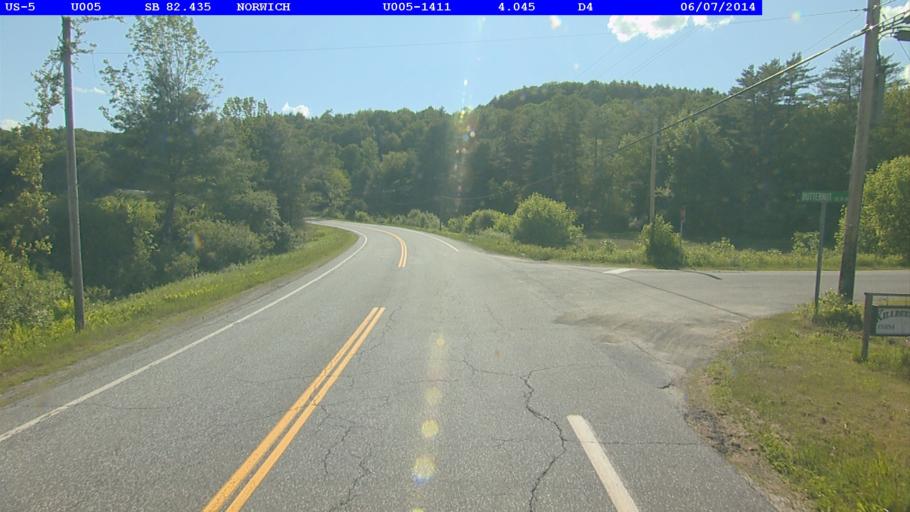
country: US
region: New Hampshire
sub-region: Grafton County
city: Hanover
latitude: 43.7350
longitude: -72.2693
